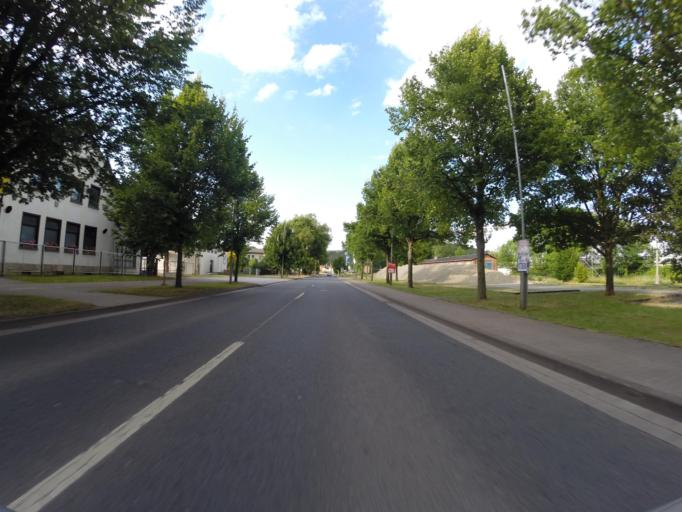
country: DE
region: Thuringia
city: Kranichfeld
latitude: 50.8575
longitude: 11.2037
